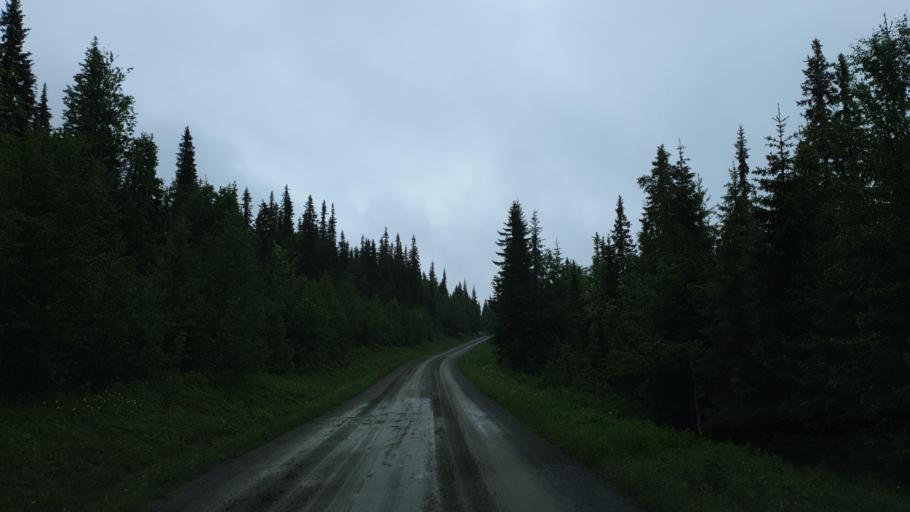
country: SE
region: Vaesterbotten
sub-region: Vilhelmina Kommun
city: Sjoberg
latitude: 65.3324
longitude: 15.9044
